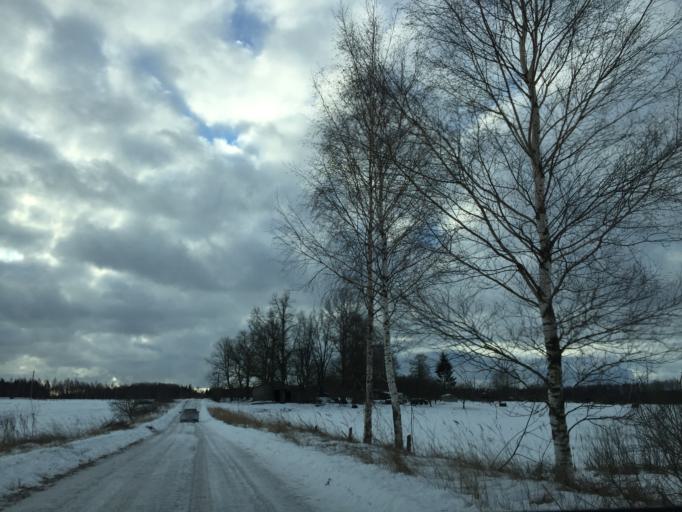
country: LV
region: Lielvarde
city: Lielvarde
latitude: 56.6251
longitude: 24.7405
